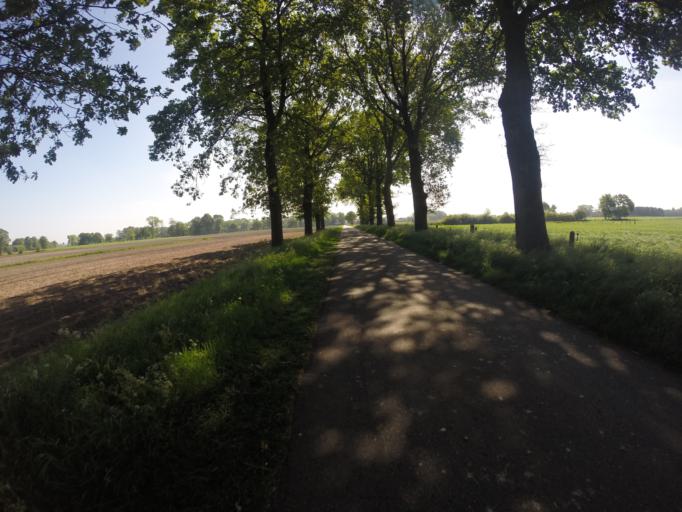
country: BE
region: Flanders
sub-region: Provincie West-Vlaanderen
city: Beernem
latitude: 51.1429
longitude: 3.3656
